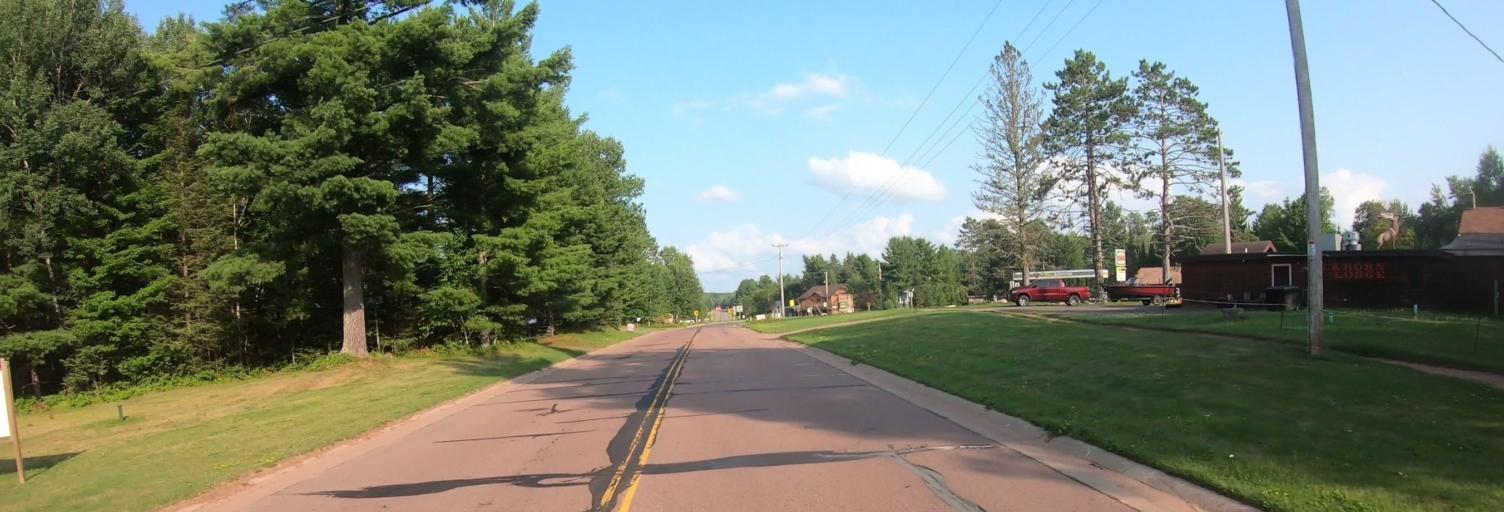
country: US
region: Wisconsin
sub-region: Ashland County
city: Ashland
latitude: 46.1736
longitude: -90.9117
